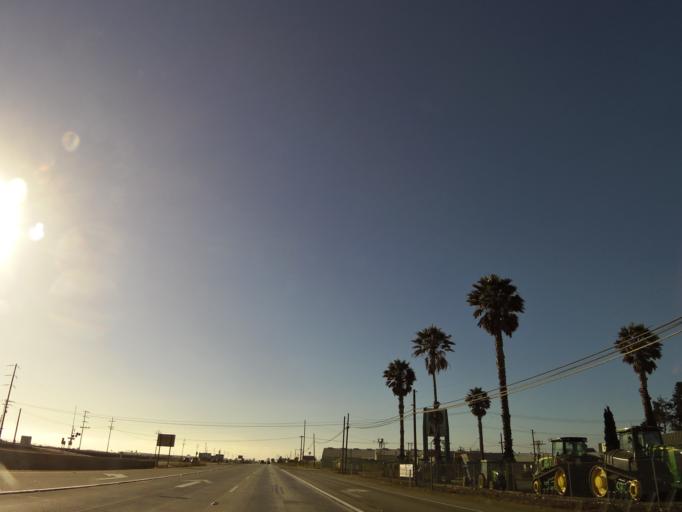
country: US
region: California
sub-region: Monterey County
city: Chualar
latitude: 36.6121
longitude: -121.5660
